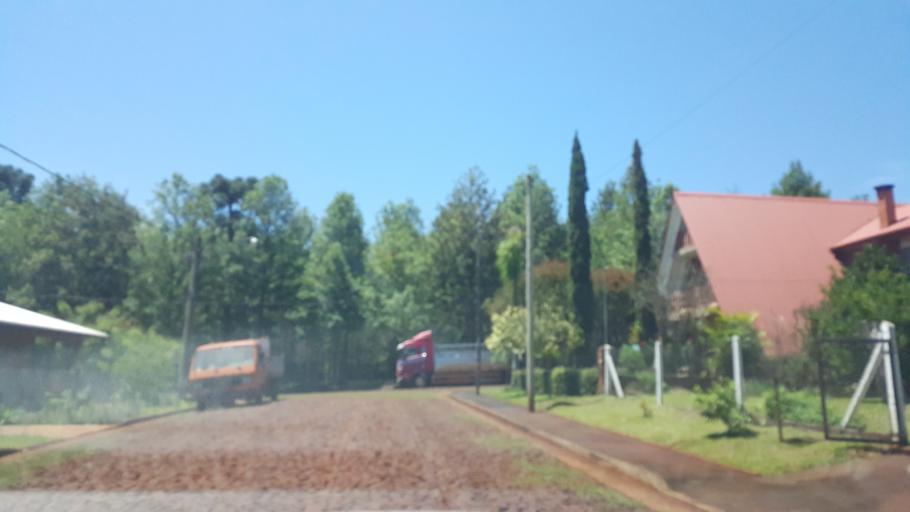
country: AR
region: Misiones
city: Capiovi
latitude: -26.9285
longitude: -55.0503
